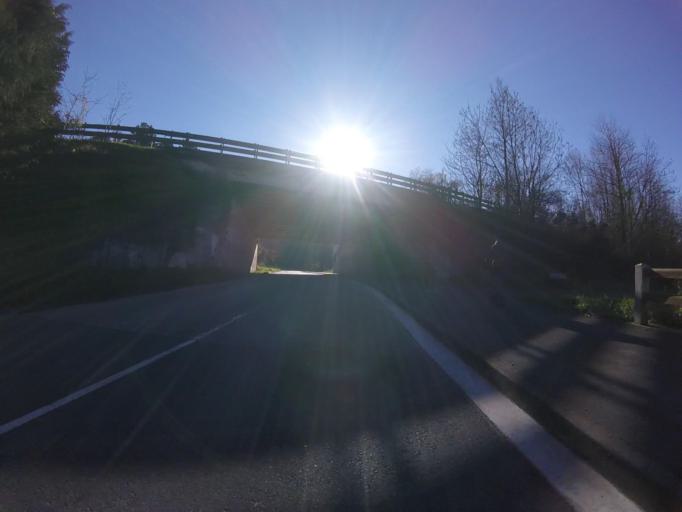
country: ES
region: Basque Country
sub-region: Provincia de Guipuzcoa
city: Irun
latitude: 43.3343
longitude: -1.7775
